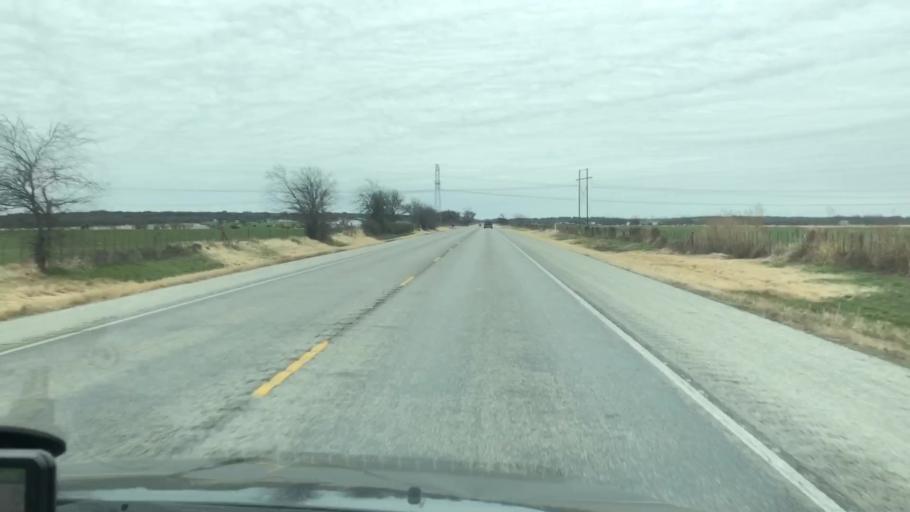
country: US
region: Texas
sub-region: Palo Pinto County
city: Mineral Wells
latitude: 32.9270
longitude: -98.0722
